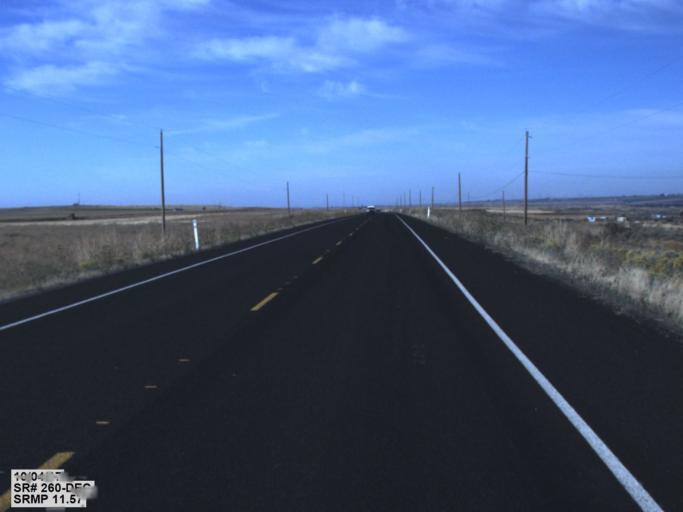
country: US
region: Washington
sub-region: Franklin County
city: Connell
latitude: 46.6347
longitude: -118.7757
